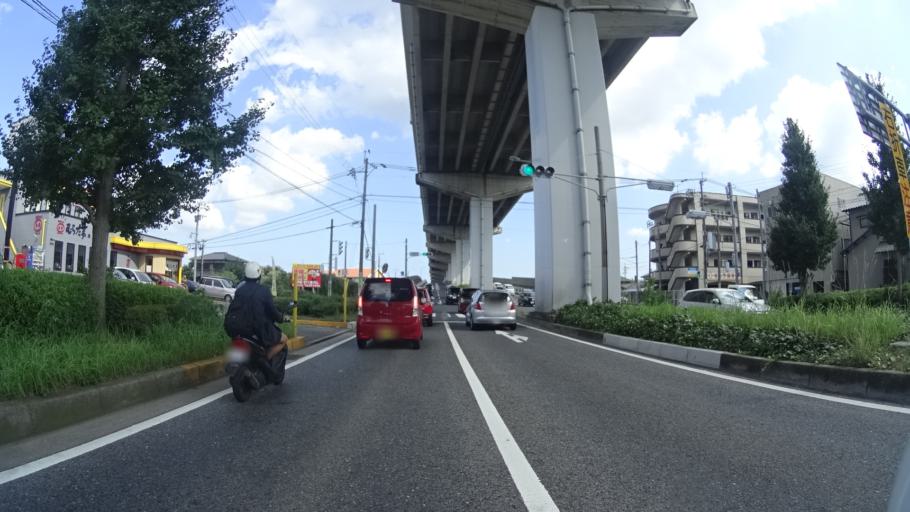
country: JP
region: Fukuoka
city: Kitakyushu
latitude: 33.8418
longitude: 130.8919
